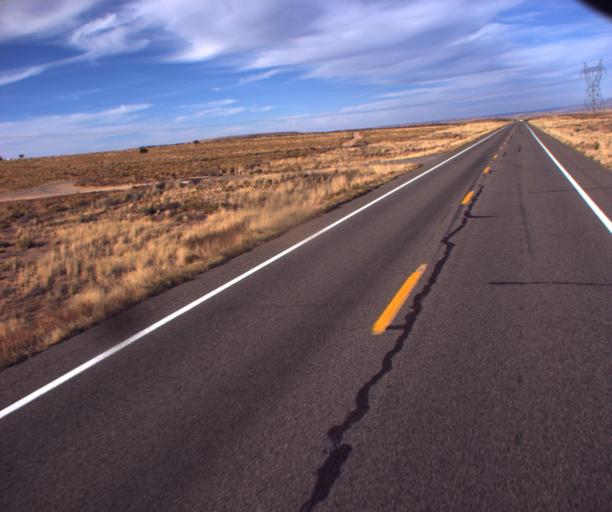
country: US
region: New Mexico
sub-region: San Juan County
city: Shiprock
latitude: 36.9583
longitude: -109.0675
